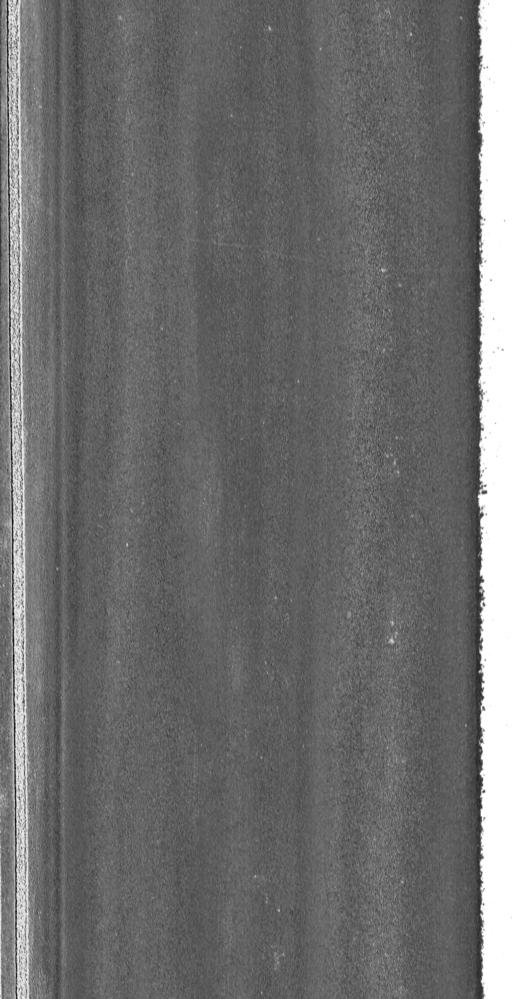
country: US
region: Vermont
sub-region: Chittenden County
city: Burlington
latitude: 44.3635
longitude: -73.2480
